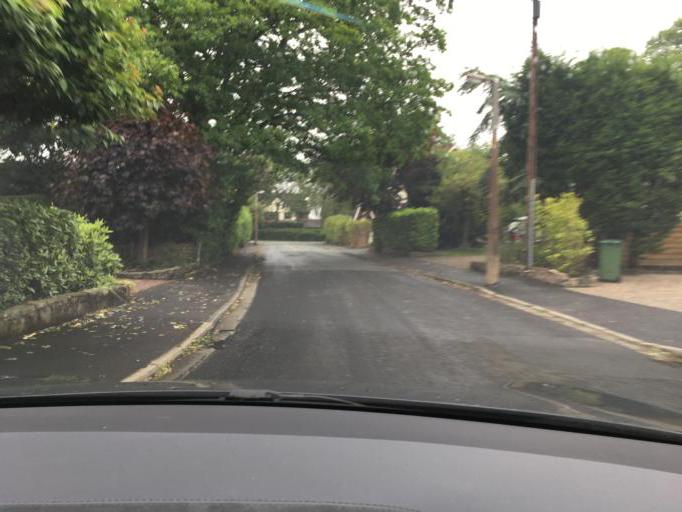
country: GB
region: England
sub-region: Borough of Stockport
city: Hazel Grove
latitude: 53.3742
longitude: -2.1366
